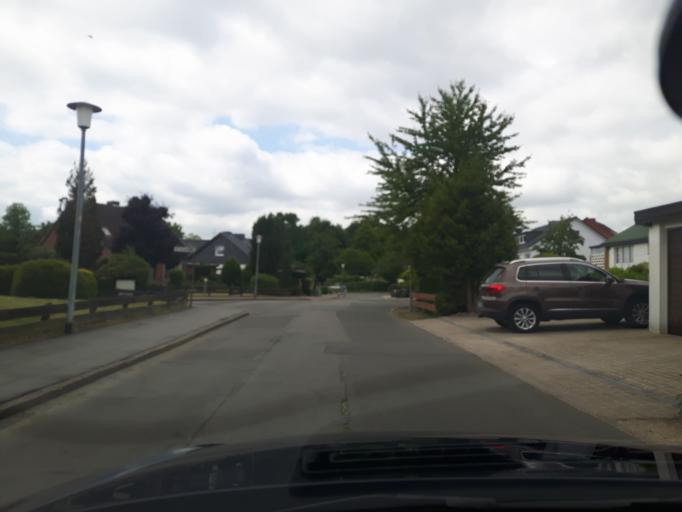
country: DE
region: Schleswig-Holstein
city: Neustadt in Holstein
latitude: 54.0927
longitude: 10.8530
